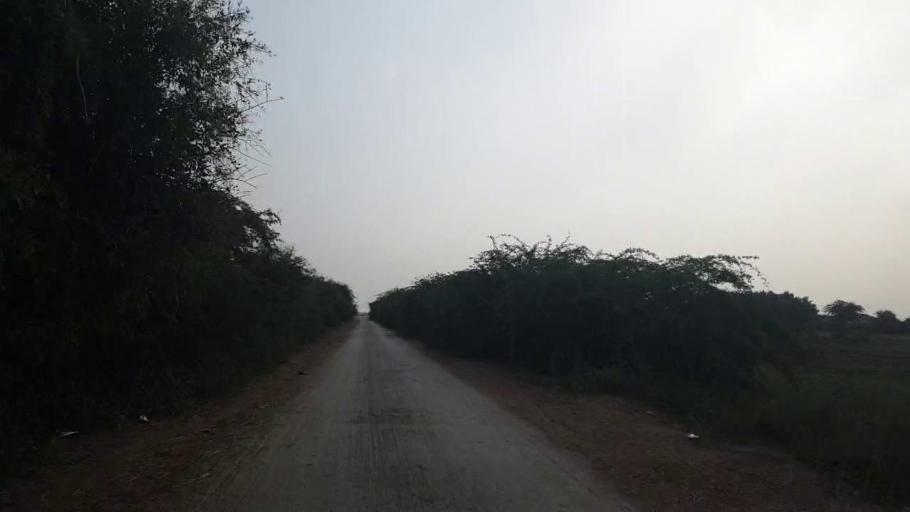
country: PK
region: Sindh
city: Badin
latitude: 24.6535
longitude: 68.7000
